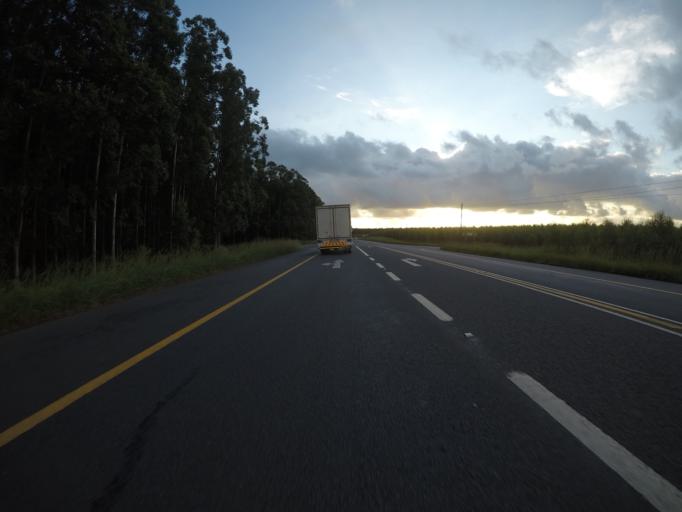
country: ZA
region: KwaZulu-Natal
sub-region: uThungulu District Municipality
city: KwaMbonambi
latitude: -28.5777
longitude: 32.1035
